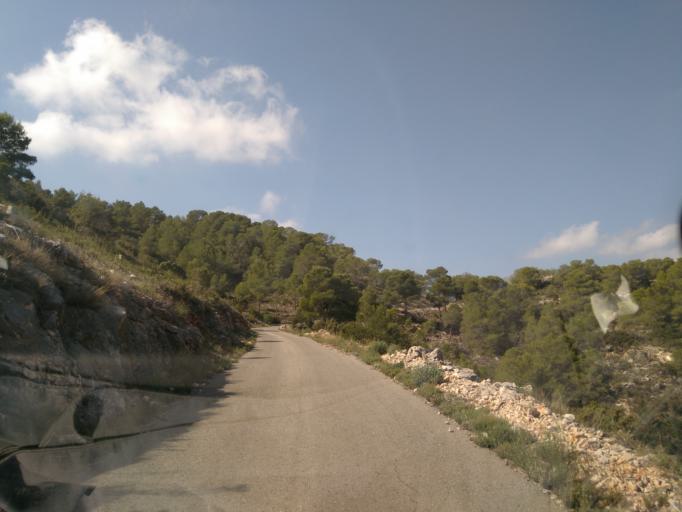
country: ES
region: Valencia
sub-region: Provincia de Valencia
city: Tous
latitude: 39.1744
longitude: -0.6126
